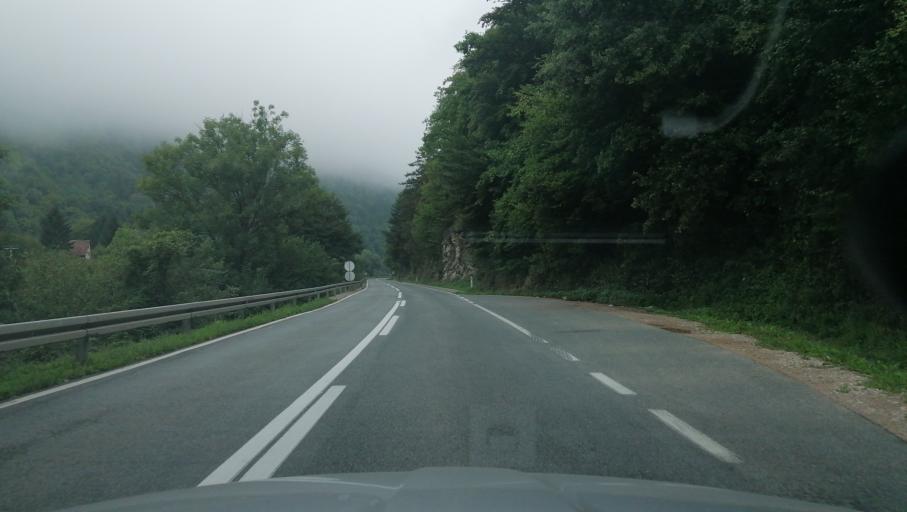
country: BA
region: Federation of Bosnia and Herzegovina
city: Donji Vakuf
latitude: 44.1614
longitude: 17.3658
